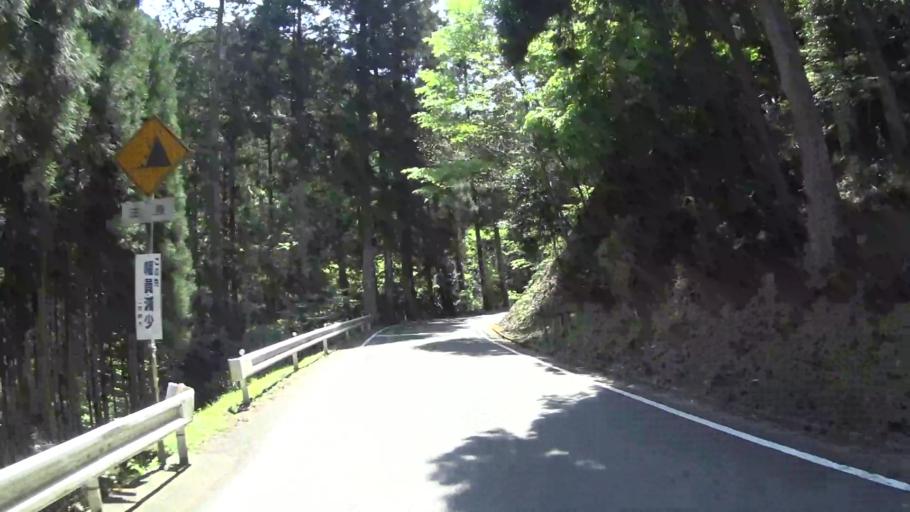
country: JP
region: Kyoto
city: Kameoka
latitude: 35.1359
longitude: 135.5888
